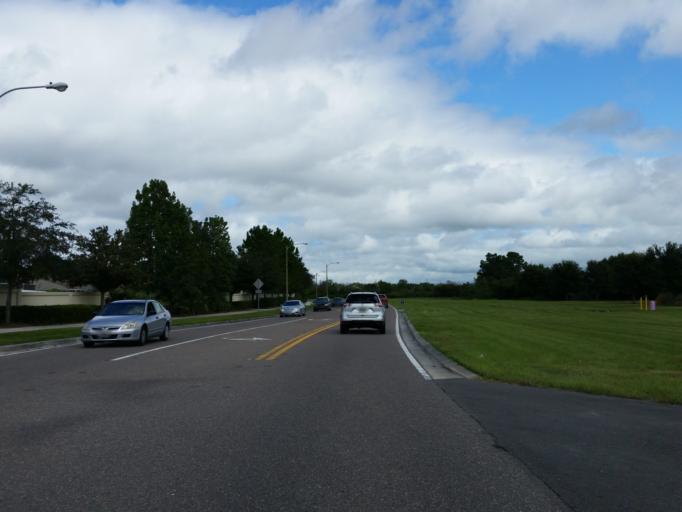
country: US
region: Florida
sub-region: Pasco County
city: Wesley Chapel
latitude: 28.2136
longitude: -82.3012
